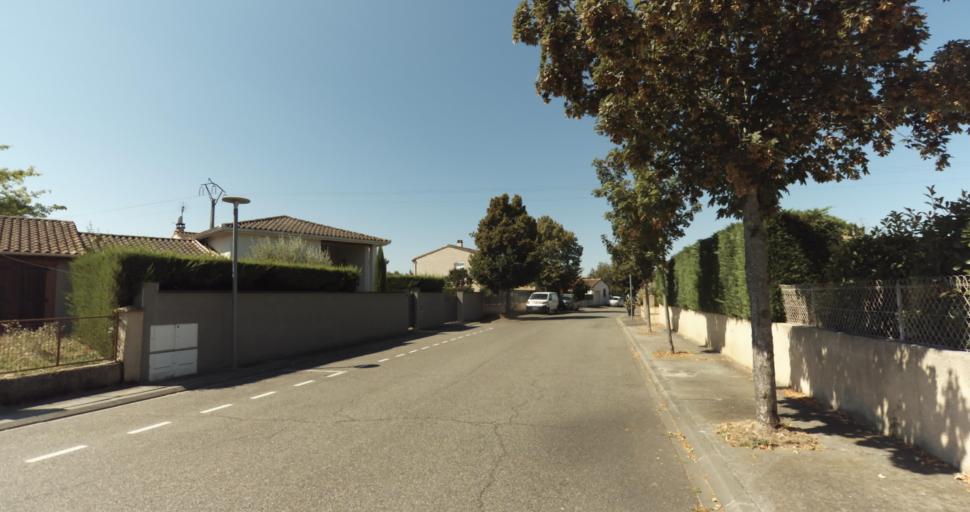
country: FR
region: Midi-Pyrenees
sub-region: Departement de la Haute-Garonne
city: L'Union
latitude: 43.6493
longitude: 1.4933
